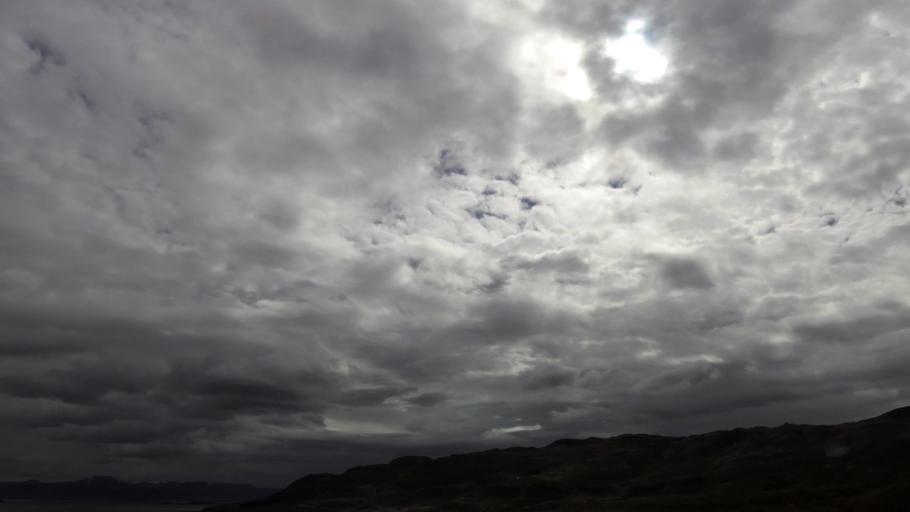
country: IS
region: West
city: Stykkisholmur
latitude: 65.5410
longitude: -22.1118
